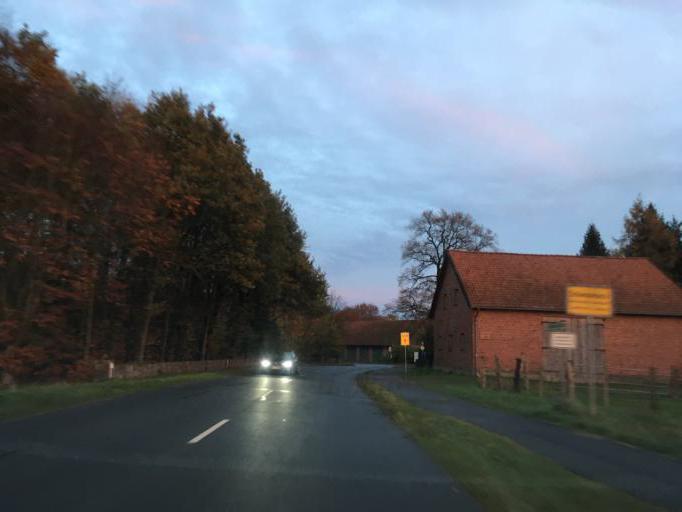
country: DE
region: Lower Saxony
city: Soderstorf
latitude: 53.1252
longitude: 10.1150
